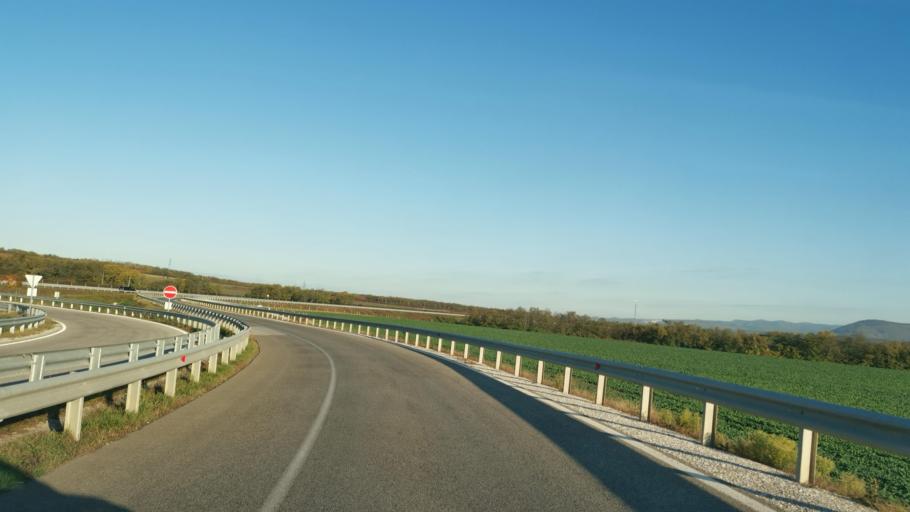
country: HU
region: Heves
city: Andornaktalya
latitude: 47.8398
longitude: 20.4005
